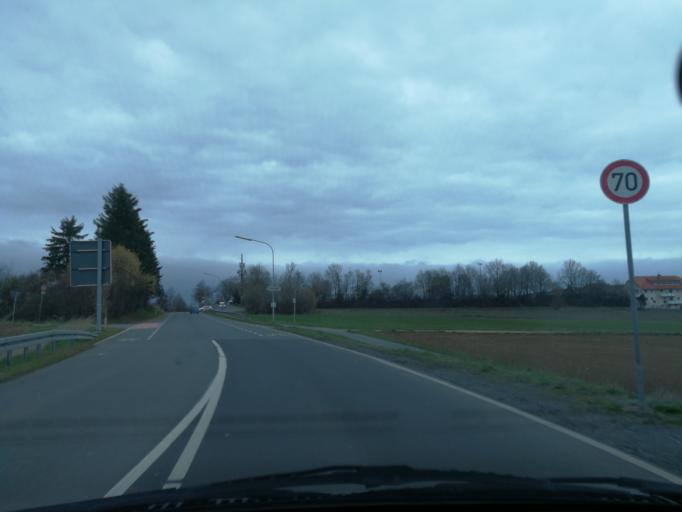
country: DE
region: Hesse
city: Reinheim
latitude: 49.8383
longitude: 8.8312
